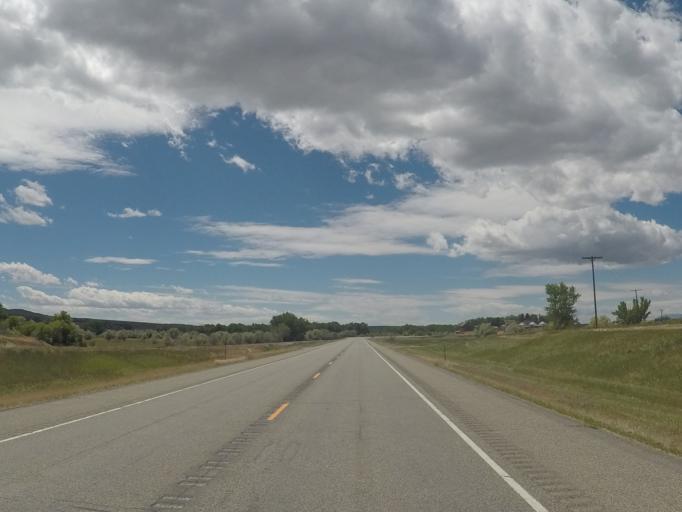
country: US
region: Montana
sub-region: Yellowstone County
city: Laurel
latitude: 45.4412
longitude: -108.8648
